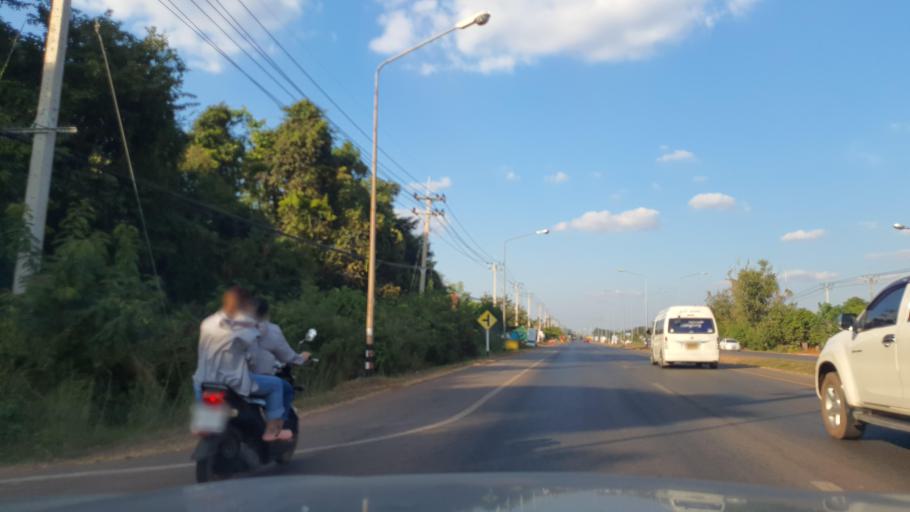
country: TH
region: Sakon Nakhon
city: Sakon Nakhon
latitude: 17.2195
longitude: 104.1045
